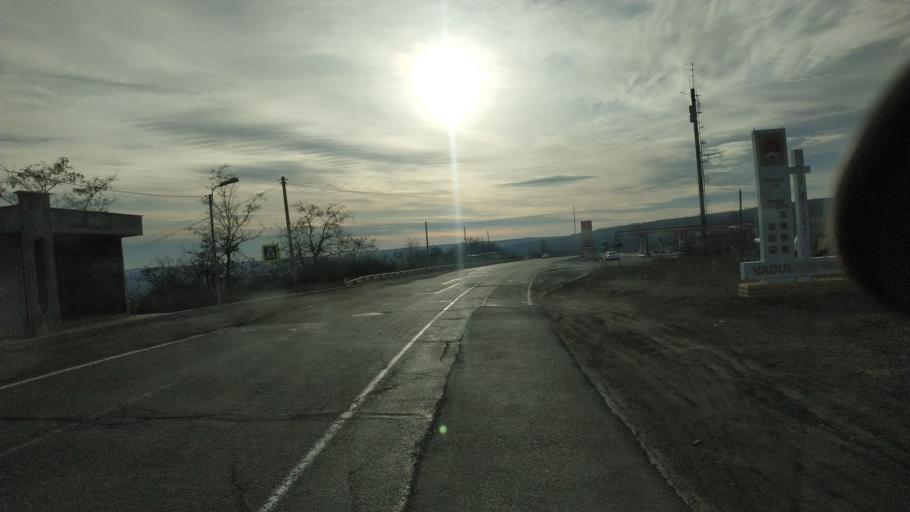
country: MD
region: Chisinau
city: Vadul lui Voda
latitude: 47.0889
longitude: 29.0699
